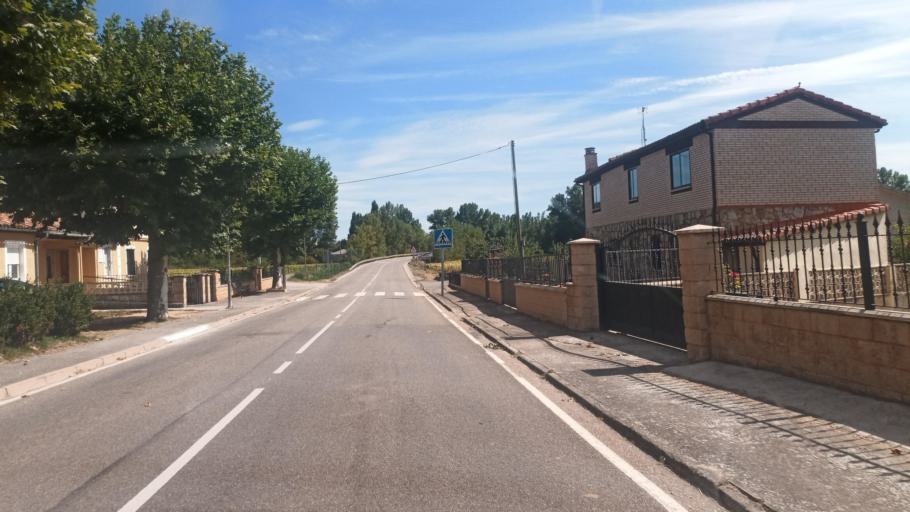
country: ES
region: Castille and Leon
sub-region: Provincia de Burgos
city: Piernigas
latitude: 42.6443
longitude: -3.3886
